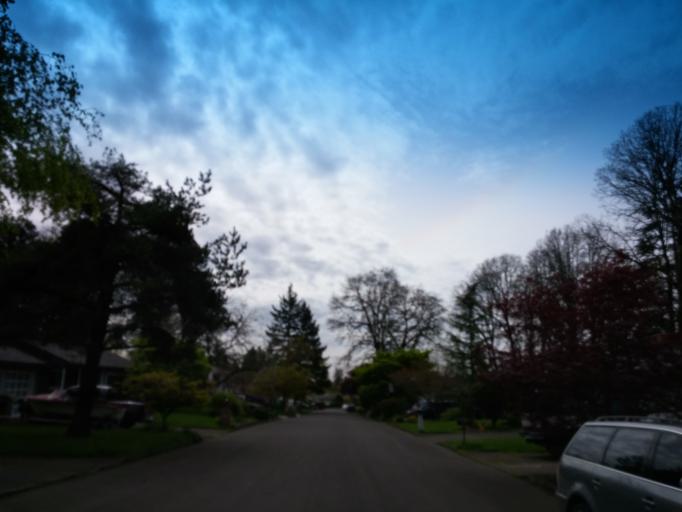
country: US
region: Oregon
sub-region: Washington County
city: Cedar Mill
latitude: 45.5322
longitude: -122.8167
